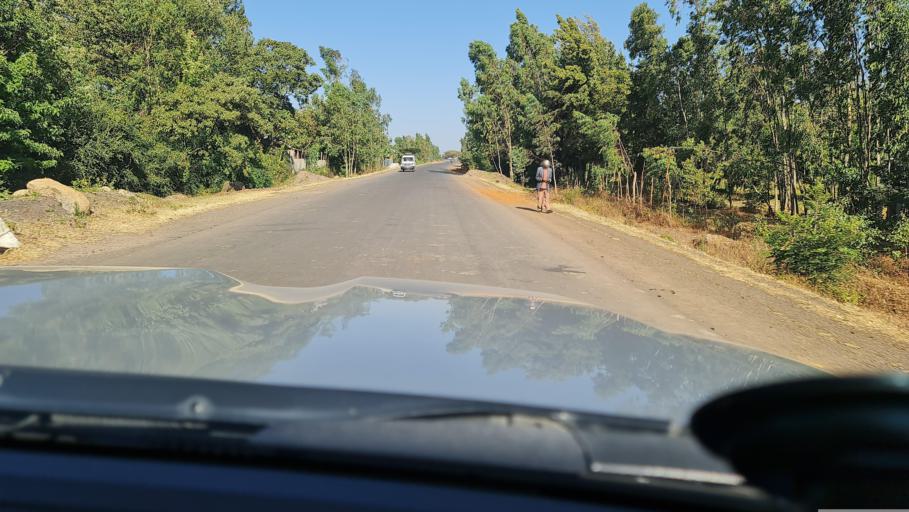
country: ET
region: Oromiya
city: Waliso
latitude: 8.5507
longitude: 37.9545
